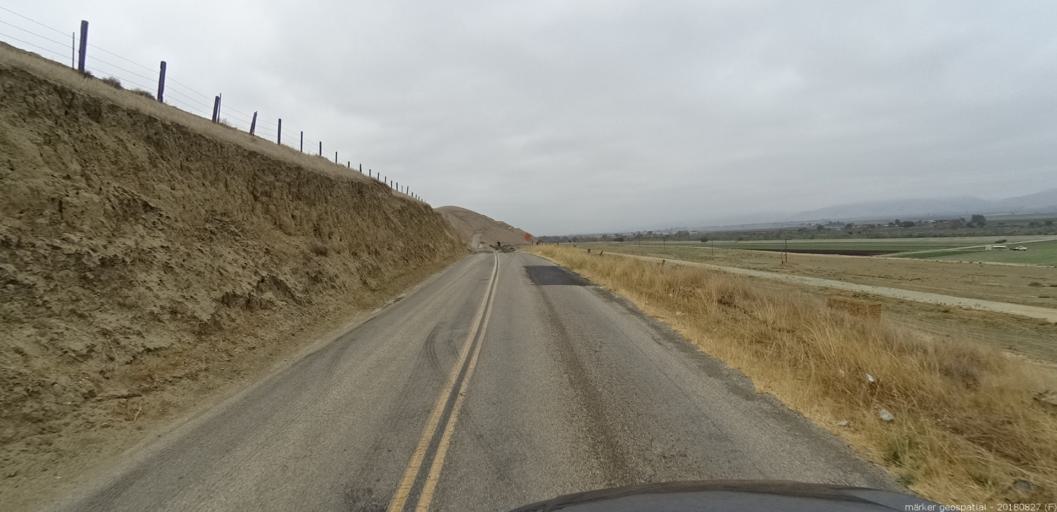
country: US
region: California
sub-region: Monterey County
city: Greenfield
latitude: 36.3289
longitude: -121.1859
